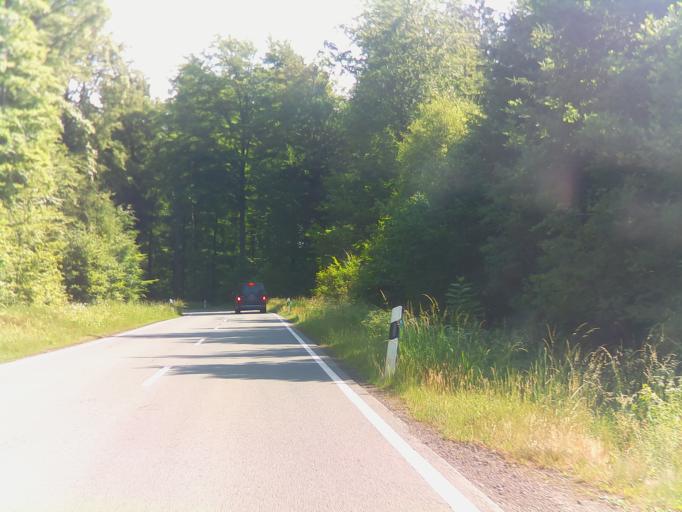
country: DE
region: Hesse
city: Rosenthal
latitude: 50.9356
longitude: 8.8423
